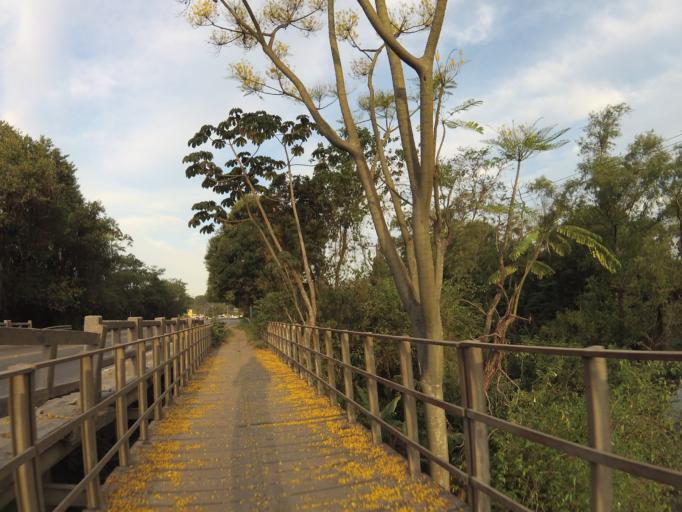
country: BR
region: Santa Catarina
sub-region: Blumenau
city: Blumenau
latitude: -26.8835
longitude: -49.1443
